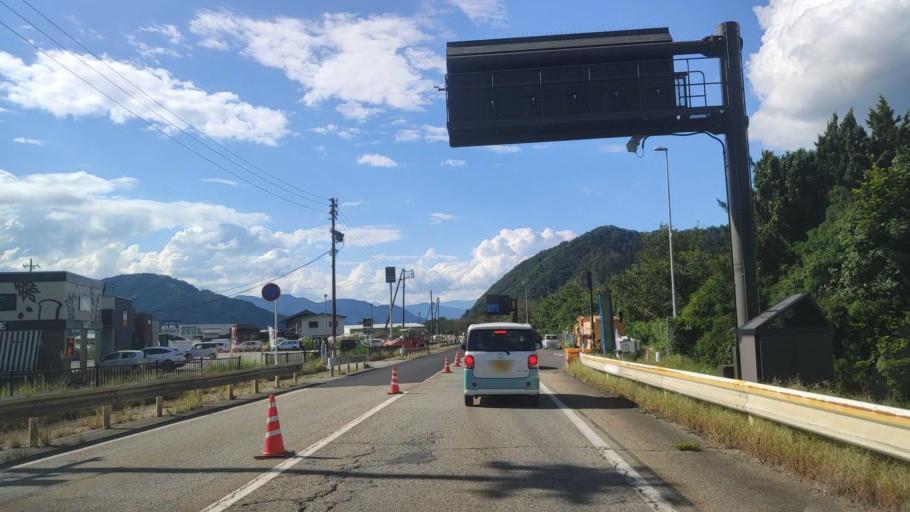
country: JP
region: Gifu
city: Takayama
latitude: 36.2023
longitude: 137.2299
